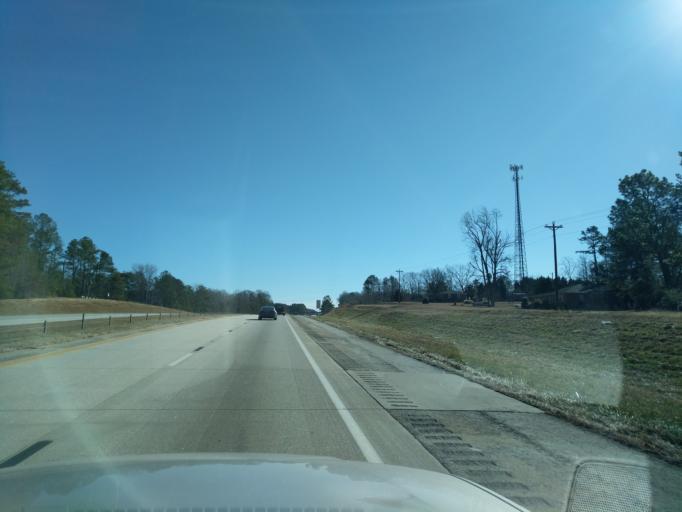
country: US
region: South Carolina
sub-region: Laurens County
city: Watts Mills
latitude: 34.5356
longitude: -81.9444
